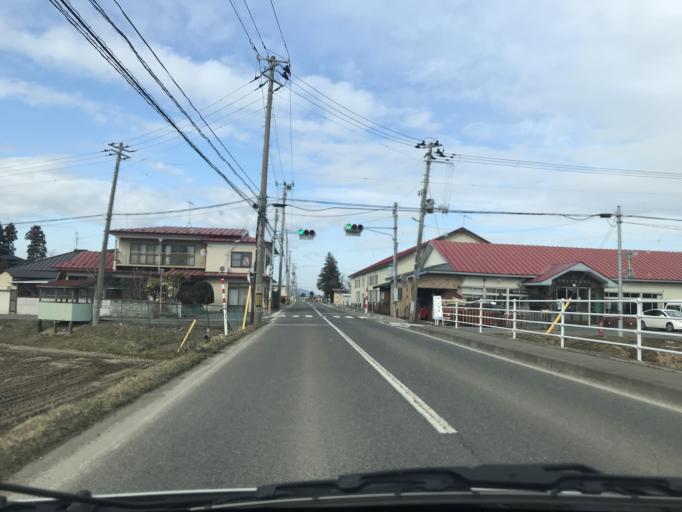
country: JP
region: Iwate
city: Hanamaki
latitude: 39.3489
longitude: 141.0481
